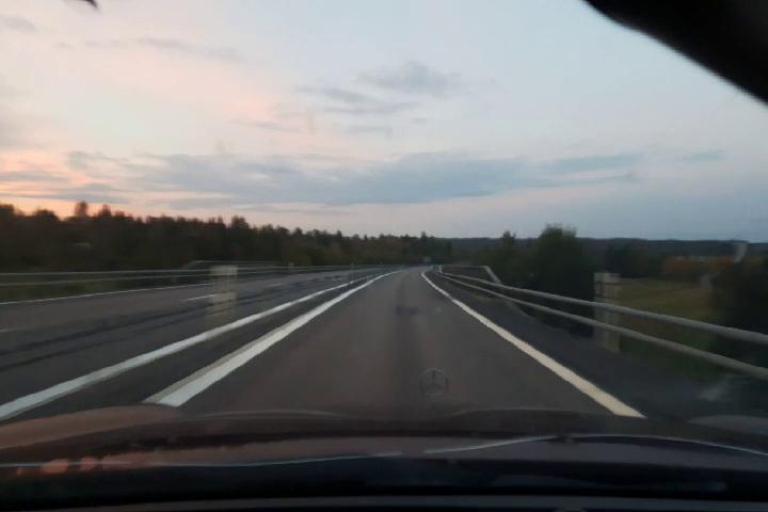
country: SE
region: Vaesternorrland
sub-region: Haernoesands Kommun
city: Haernoesand
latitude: 62.8723
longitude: 18.0457
